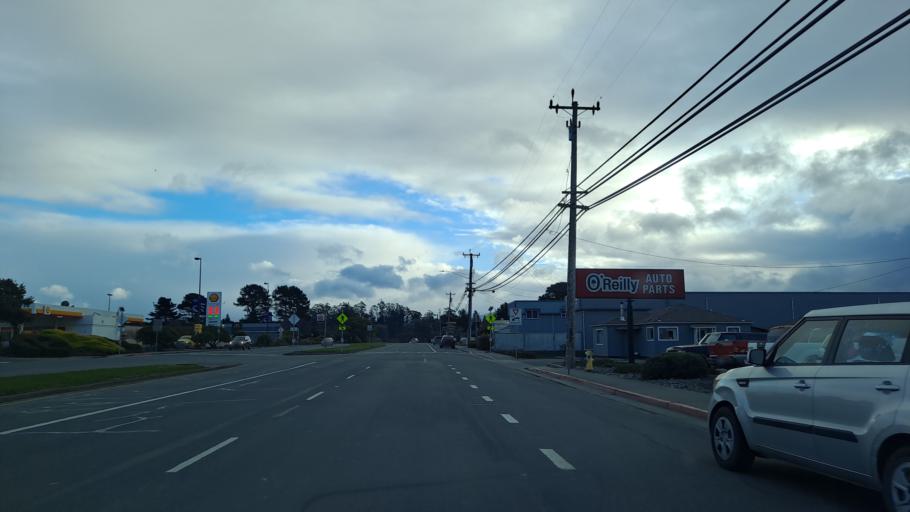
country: US
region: California
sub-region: Humboldt County
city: Fortuna
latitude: 40.5841
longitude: -124.1469
